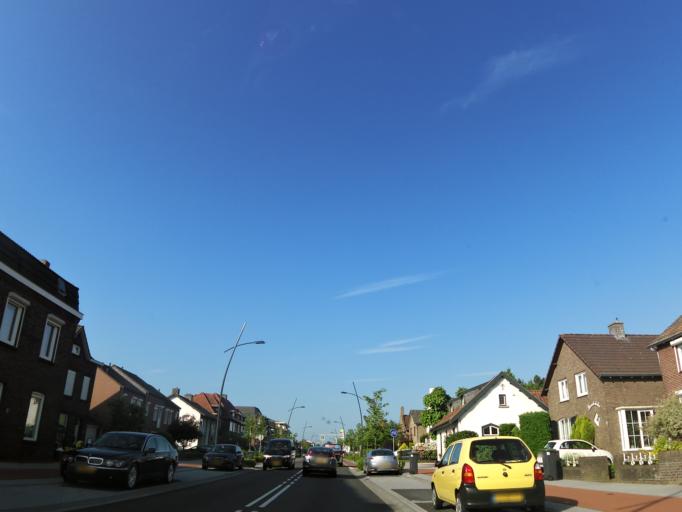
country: NL
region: Limburg
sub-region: Gemeente Beek
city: Beek
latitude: 50.9442
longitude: 5.7986
